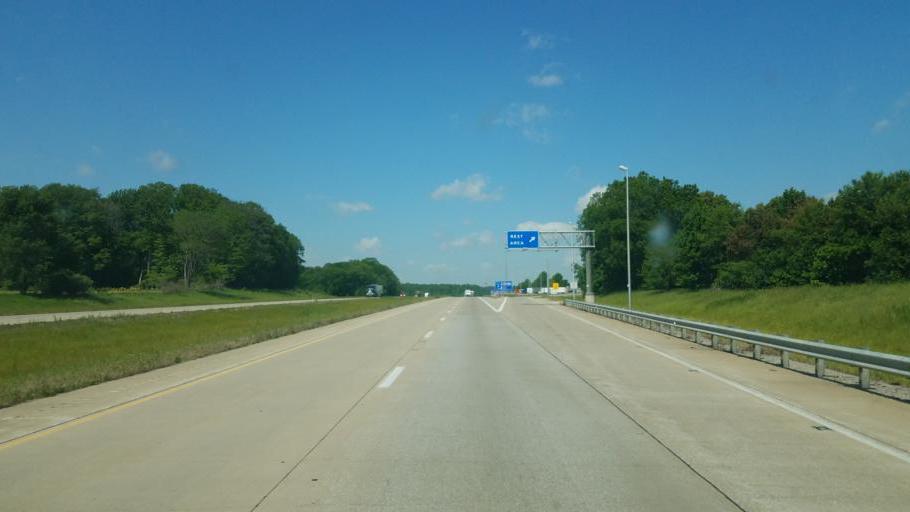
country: US
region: Illinois
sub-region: Clark County
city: Marshall
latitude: 39.4220
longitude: -87.6548
